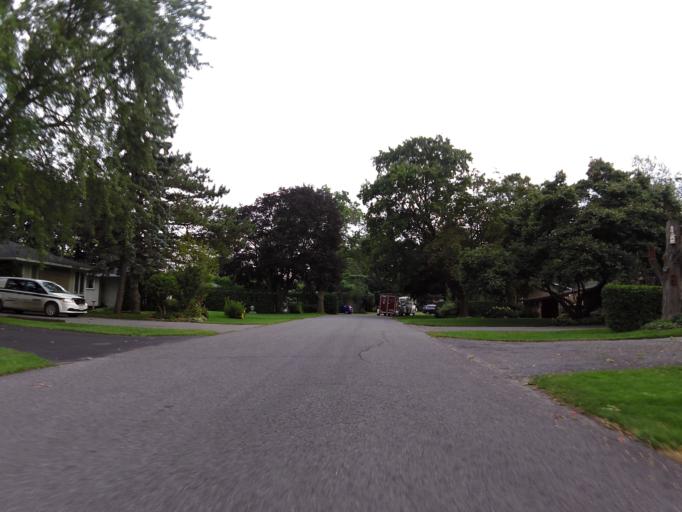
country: CA
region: Ontario
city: Bells Corners
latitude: 45.3178
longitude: -75.8194
